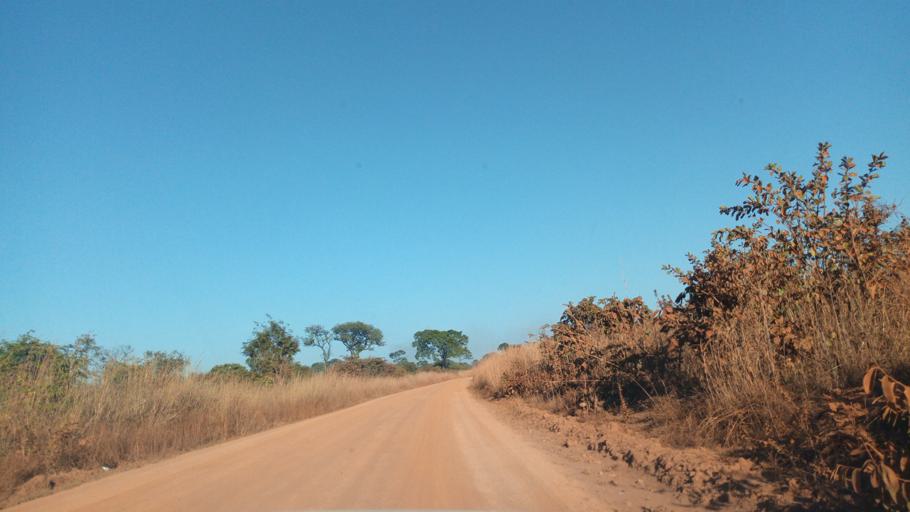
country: ZM
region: Luapula
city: Mwense
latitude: -10.4837
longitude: 28.5031
